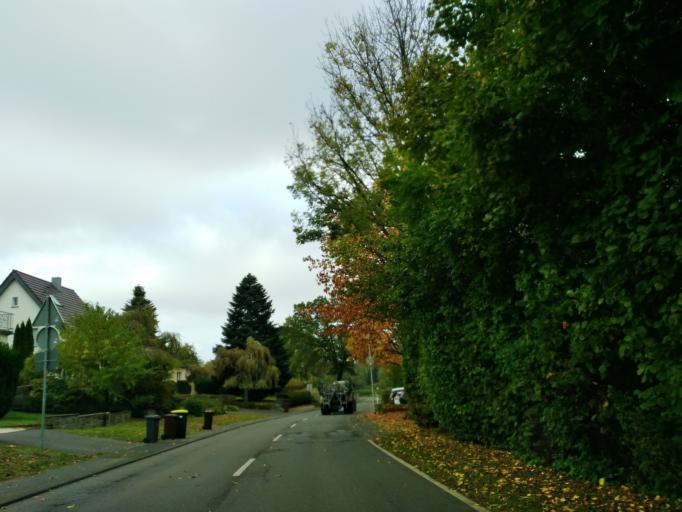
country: DE
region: North Rhine-Westphalia
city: Sankt Augustin
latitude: 50.7317
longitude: 7.2189
